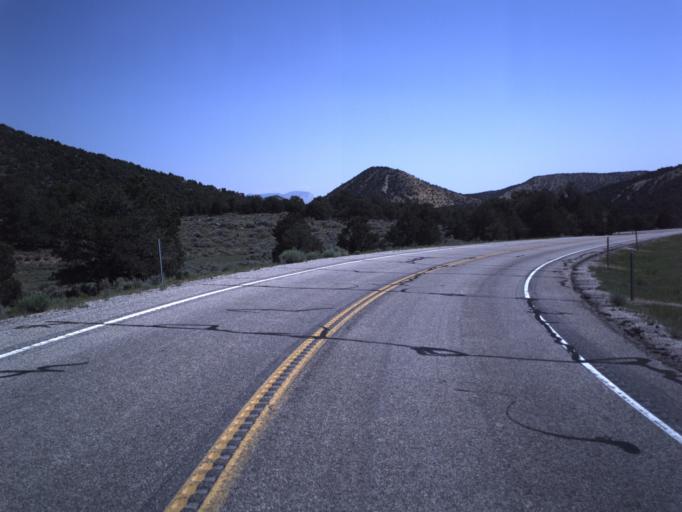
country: US
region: Utah
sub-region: Wayne County
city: Loa
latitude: 38.7275
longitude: -111.4011
